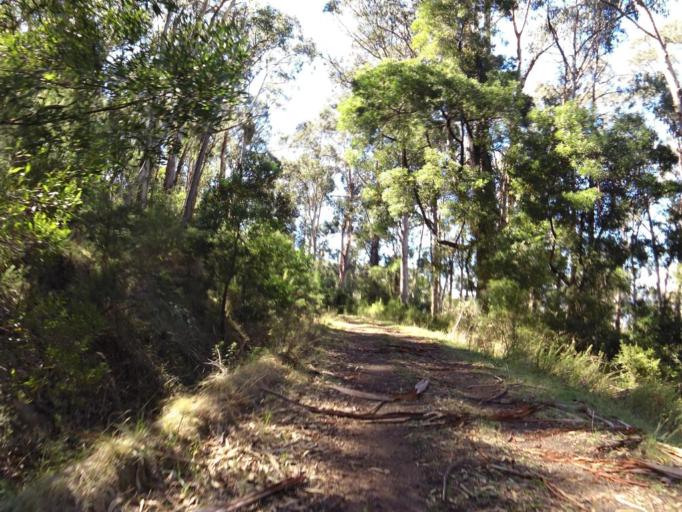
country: AU
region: Victoria
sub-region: Yarra Ranges
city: Launching Place
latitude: -37.7416
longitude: 145.5753
